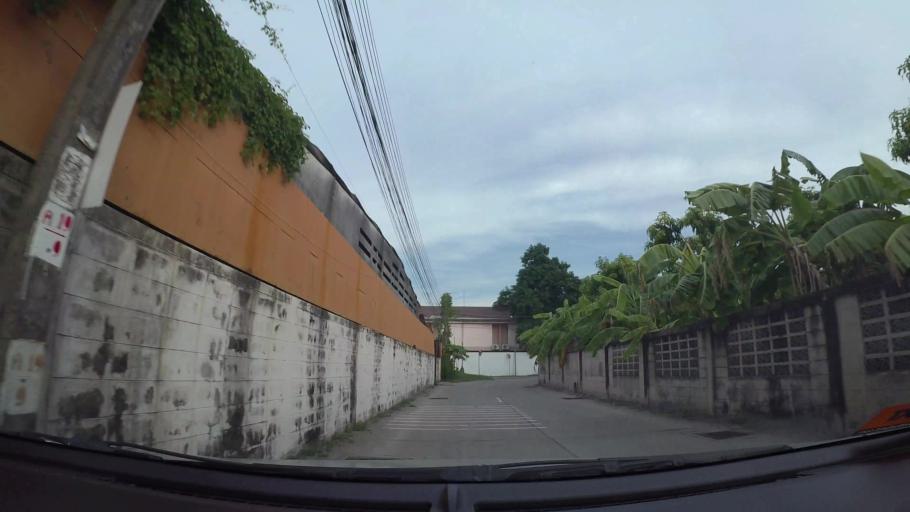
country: TH
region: Chon Buri
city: Chon Buri
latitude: 13.3335
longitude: 100.9795
